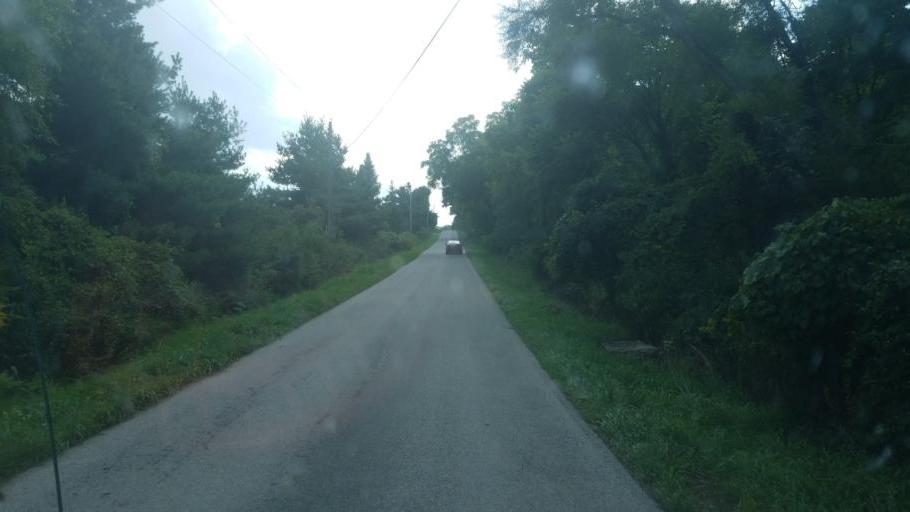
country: US
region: Ohio
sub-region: Huron County
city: Plymouth
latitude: 41.0147
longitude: -82.6513
